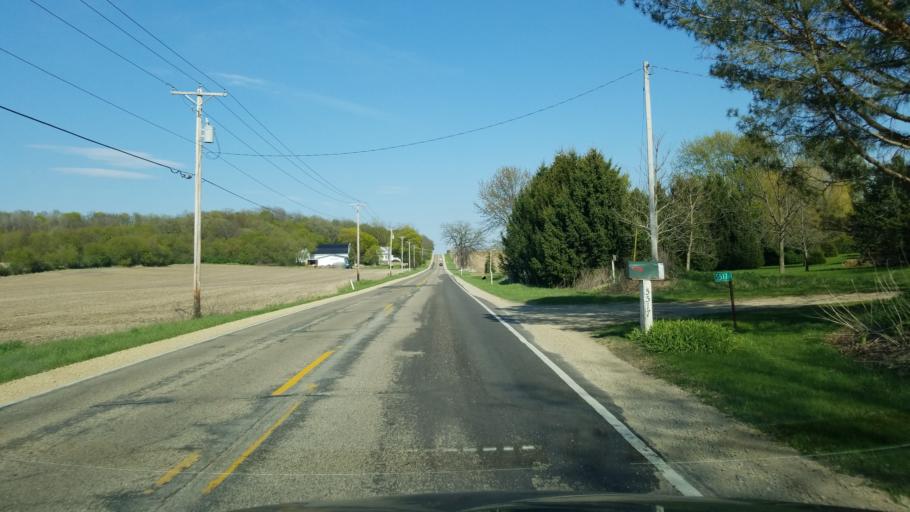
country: US
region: Wisconsin
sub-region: Dane County
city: Oregon
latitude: 42.9291
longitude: -89.4264
